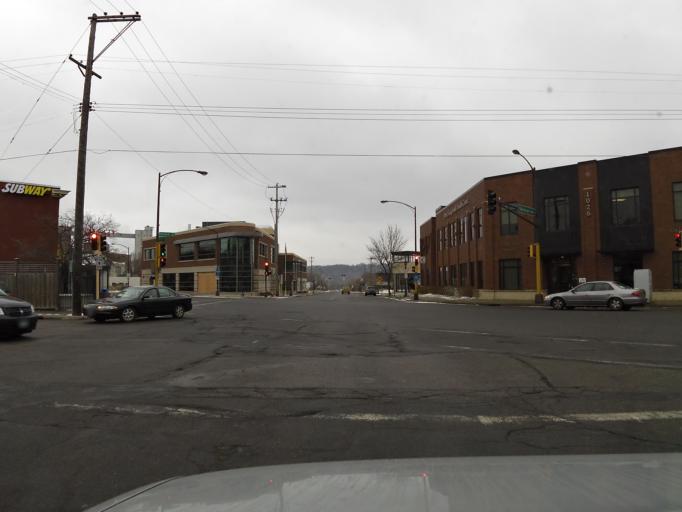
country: US
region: Minnesota
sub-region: Dakota County
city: West Saint Paul
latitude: 44.9268
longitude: -93.1284
